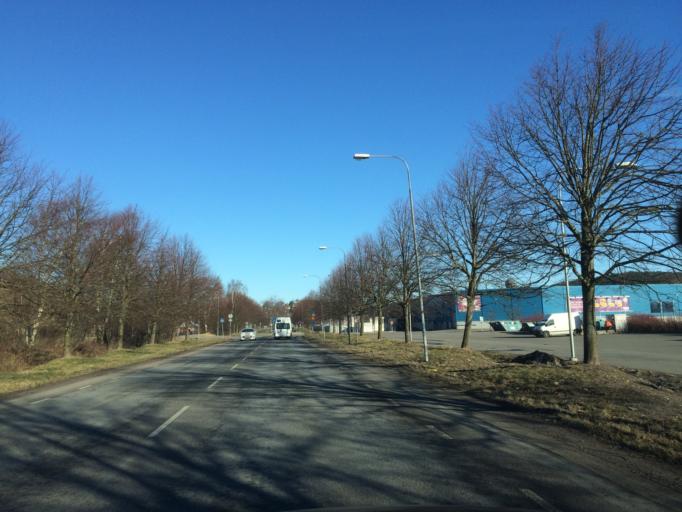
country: SE
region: Vaestra Goetaland
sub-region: Molndal
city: Kallered
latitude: 57.6041
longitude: 12.0461
